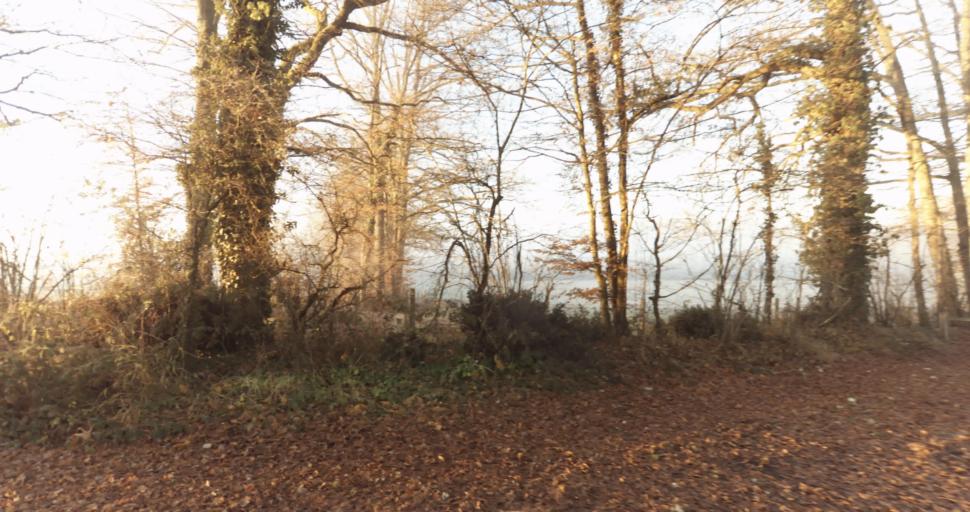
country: FR
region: Limousin
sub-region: Departement de la Haute-Vienne
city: Saint-Priest-sous-Aixe
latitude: 45.8249
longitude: 1.1226
